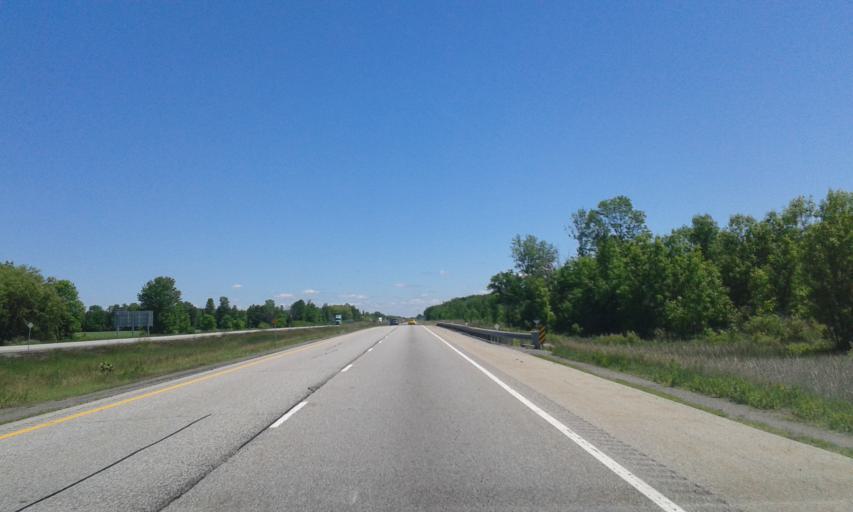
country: US
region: New York
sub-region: St. Lawrence County
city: Ogdensburg
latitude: 44.8636
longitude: -75.3180
